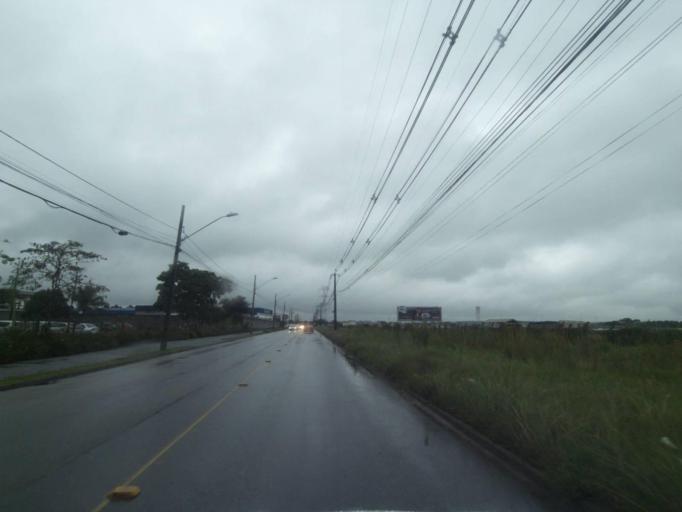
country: BR
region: Parana
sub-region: Araucaria
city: Araucaria
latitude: -25.5365
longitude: -49.3327
